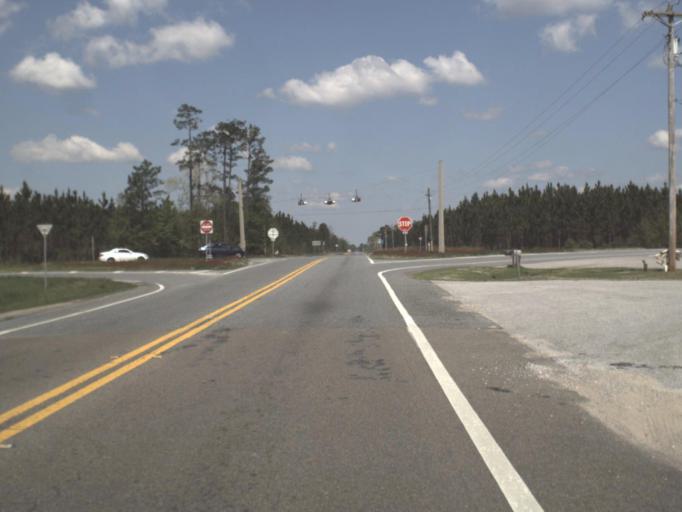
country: US
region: Alabama
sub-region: Escambia County
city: East Brewton
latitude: 30.9054
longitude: -87.0338
